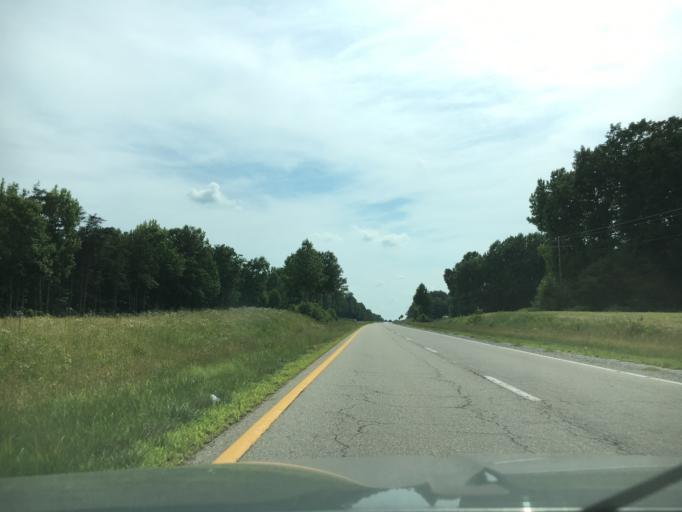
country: US
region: Virginia
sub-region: Nottoway County
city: Crewe
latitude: 37.1547
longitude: -78.2776
